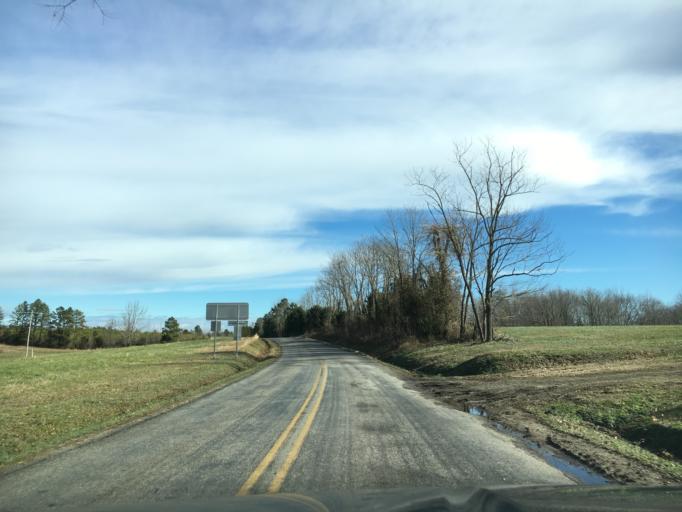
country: US
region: Virginia
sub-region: Nottoway County
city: Crewe
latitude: 37.3283
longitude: -78.1668
